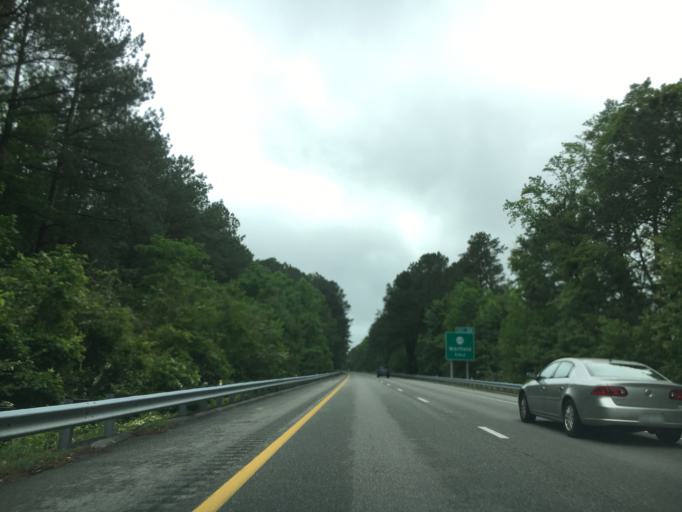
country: US
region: Virginia
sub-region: Brunswick County
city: Lawrenceville
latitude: 36.9069
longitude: -77.7858
